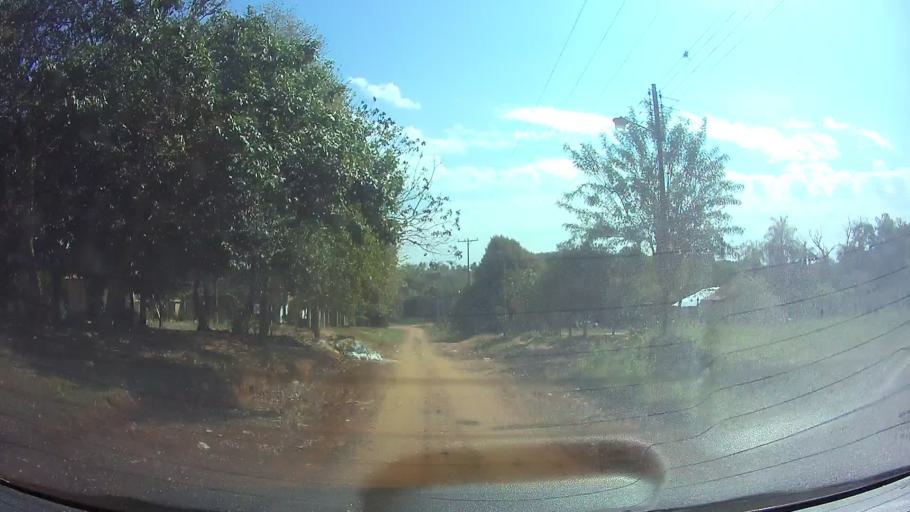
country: PY
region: Central
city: Limpio
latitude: -25.2266
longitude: -57.4385
